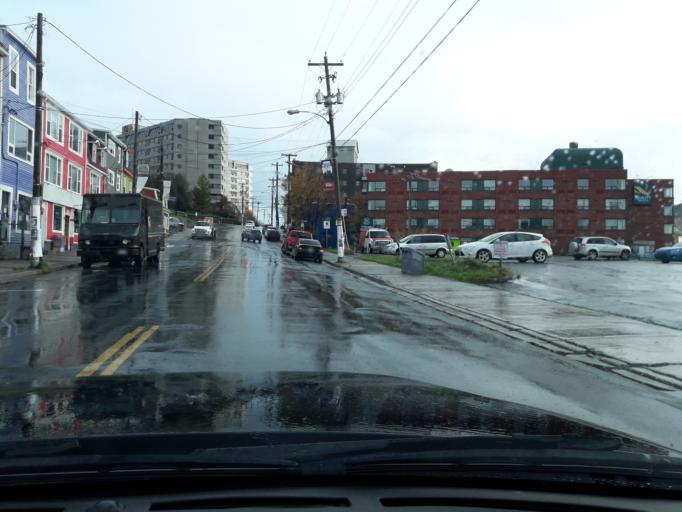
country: CA
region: Newfoundland and Labrador
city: St. John's
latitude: 47.5696
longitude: -52.7016
